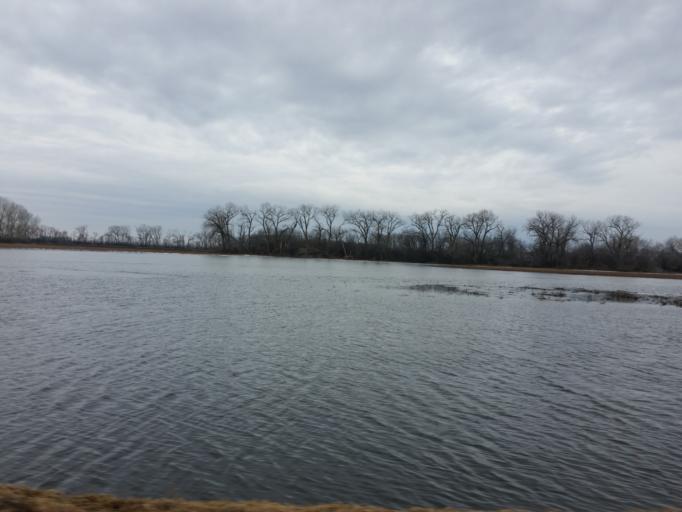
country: US
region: North Dakota
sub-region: Walsh County
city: Grafton
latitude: 48.4031
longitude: -97.4702
